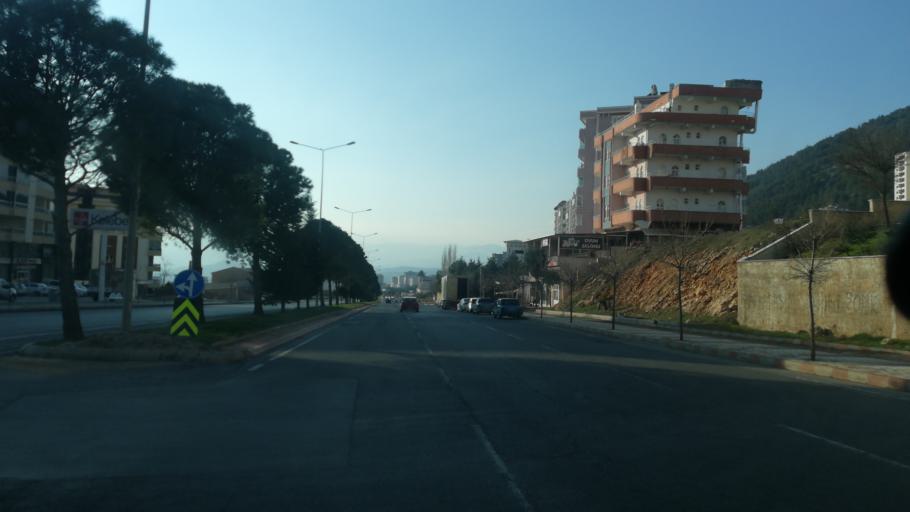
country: TR
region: Kahramanmaras
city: Kahramanmaras
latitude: 37.5976
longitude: 36.8458
